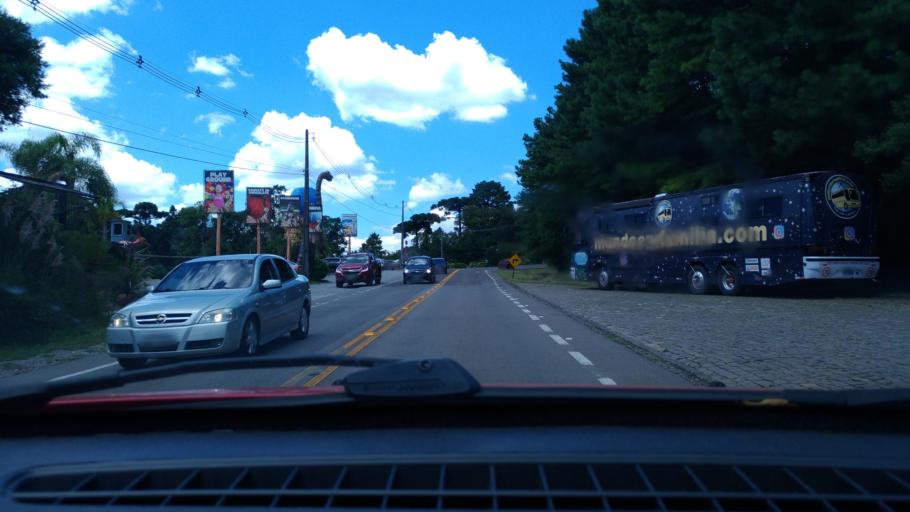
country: BR
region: Rio Grande do Sul
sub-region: Canela
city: Canela
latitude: -29.3497
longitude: -50.8339
